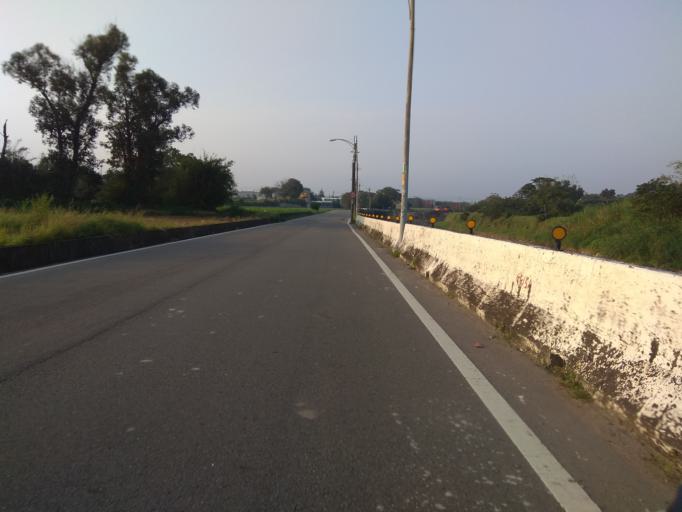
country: TW
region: Taiwan
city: Daxi
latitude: 24.9377
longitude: 121.2115
